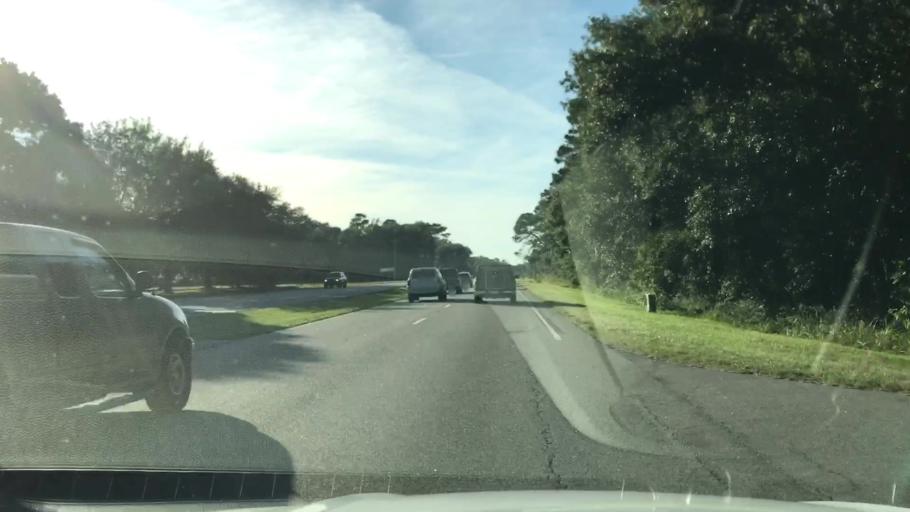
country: US
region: South Carolina
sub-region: Charleston County
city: Shell Point
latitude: 32.7953
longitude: -80.0687
